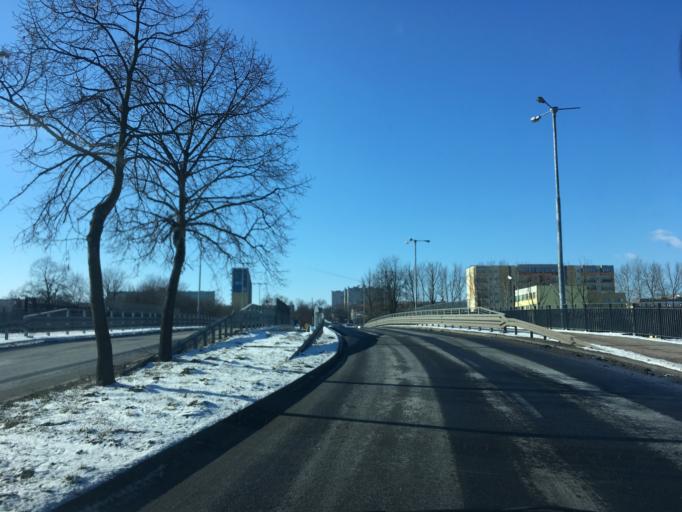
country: PL
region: Pomeranian Voivodeship
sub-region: Slupsk
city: Slupsk
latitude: 54.4726
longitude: 17.0182
